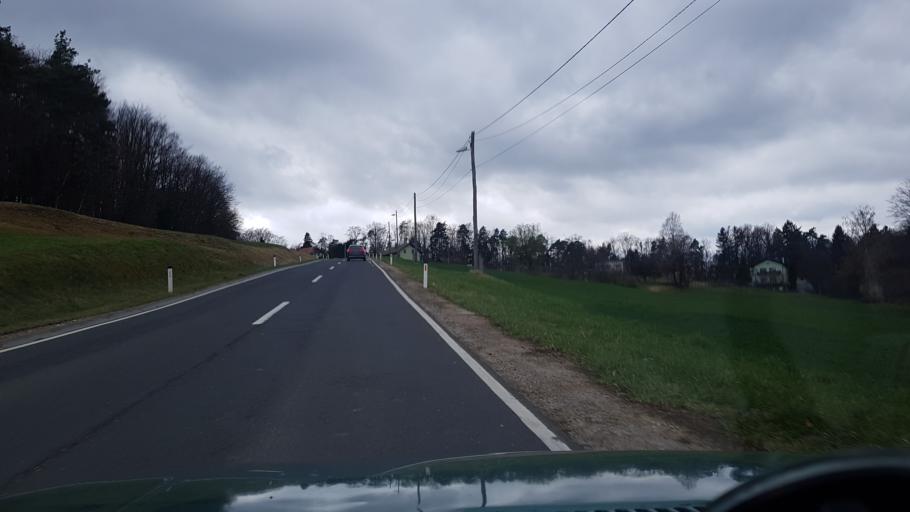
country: SI
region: Slovenska Bistrica
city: Slovenska Bistrica
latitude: 46.3732
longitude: 15.5302
